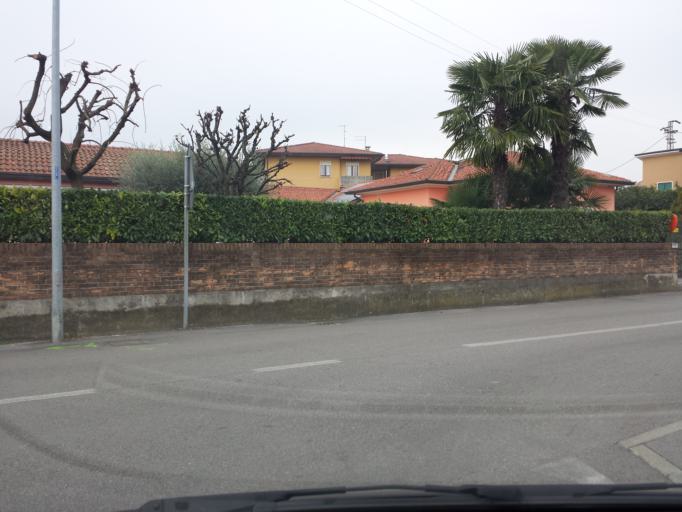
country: IT
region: Veneto
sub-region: Provincia di Vicenza
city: Sandrigo
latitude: 45.6647
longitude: 11.5979
